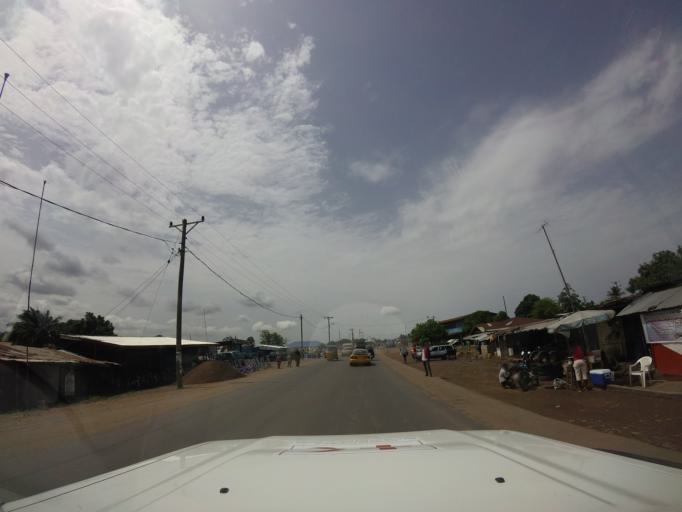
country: LR
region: Montserrado
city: Monrovia
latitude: 6.3858
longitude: -10.7815
